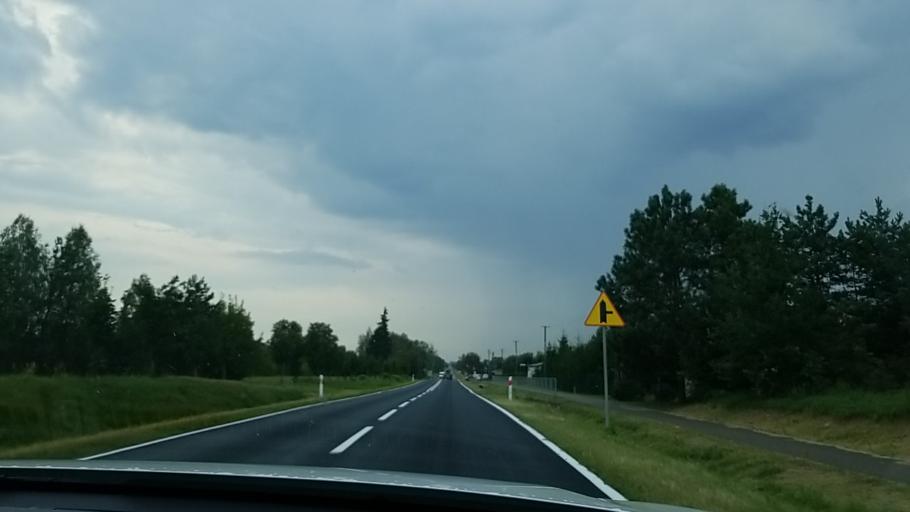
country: PL
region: Lublin Voivodeship
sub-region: Powiat wlodawski
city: Wlodawa
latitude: 51.5748
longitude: 23.5454
